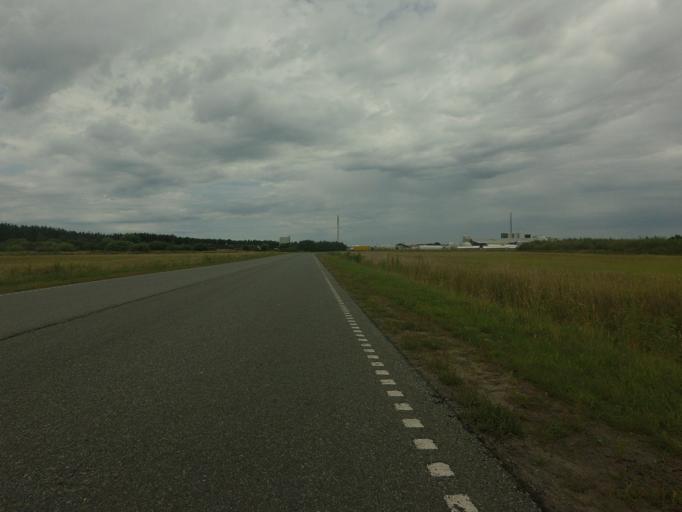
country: DK
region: North Denmark
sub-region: Jammerbugt Kommune
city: Pandrup
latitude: 57.3672
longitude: 9.7293
